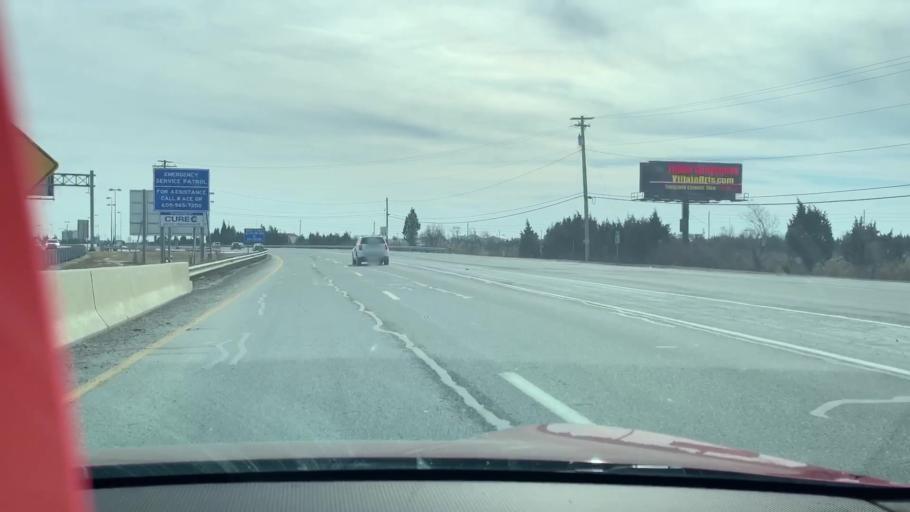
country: US
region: New Jersey
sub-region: Atlantic County
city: Pleasantville
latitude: 39.3901
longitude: -74.5095
